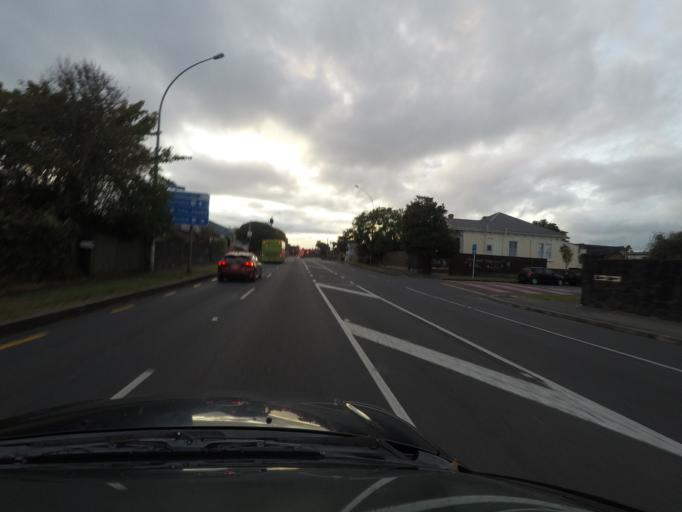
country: NZ
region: Auckland
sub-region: Auckland
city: Auckland
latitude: -36.8864
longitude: 174.7443
